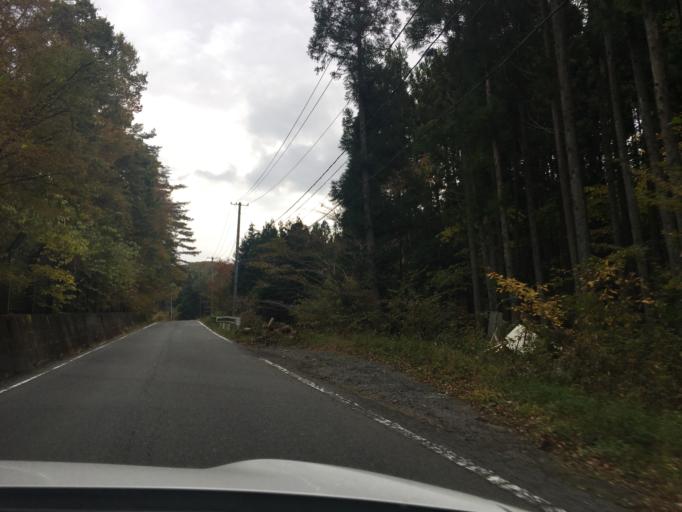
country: JP
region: Fukushima
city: Iwaki
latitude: 37.1187
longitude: 140.7783
